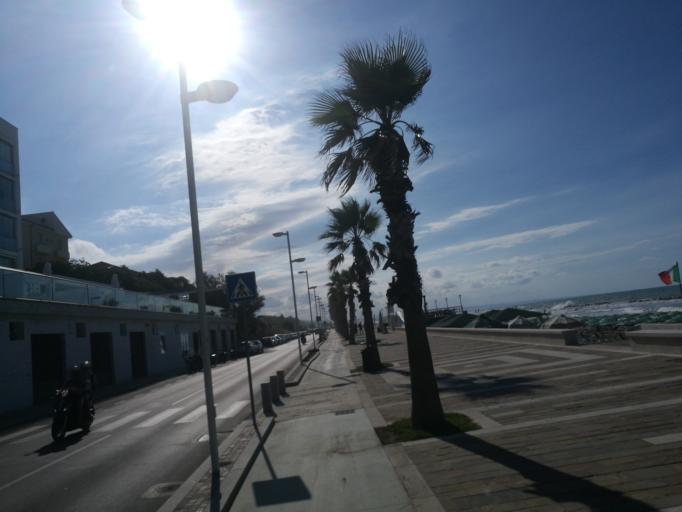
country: IT
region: Molise
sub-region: Provincia di Campobasso
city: Termoli
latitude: 42.0060
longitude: 14.9822
